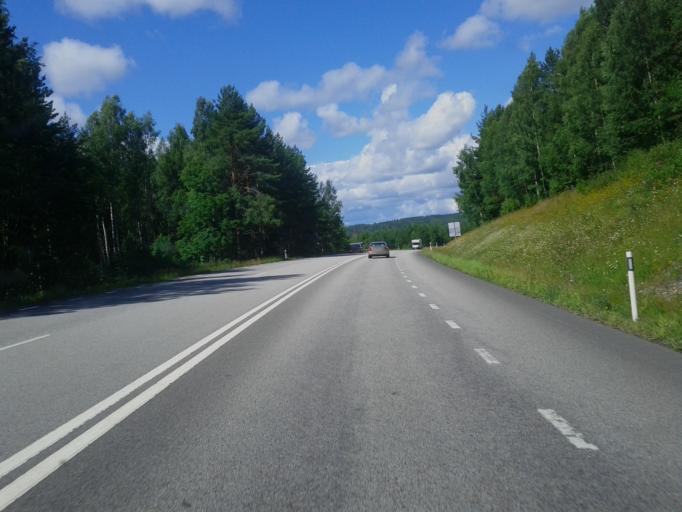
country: SE
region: Dalarna
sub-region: Rattviks Kommun
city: Vikarbyn
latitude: 60.9078
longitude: 15.0613
